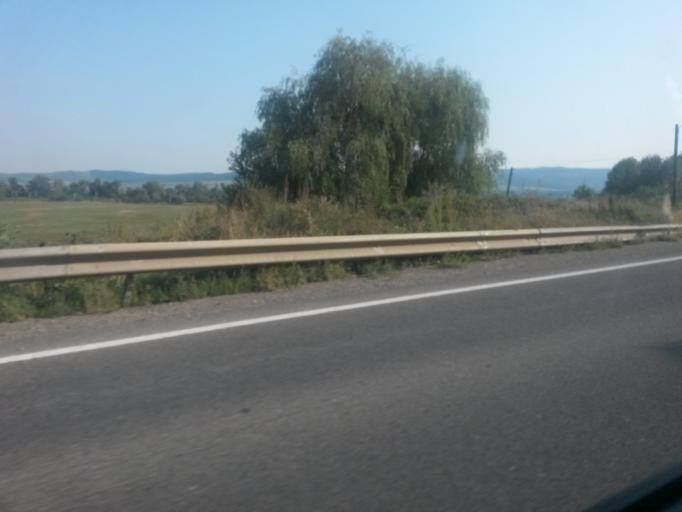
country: RO
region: Alba
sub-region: Comuna Unirea
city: Unirea
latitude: 46.3934
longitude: 23.7919
